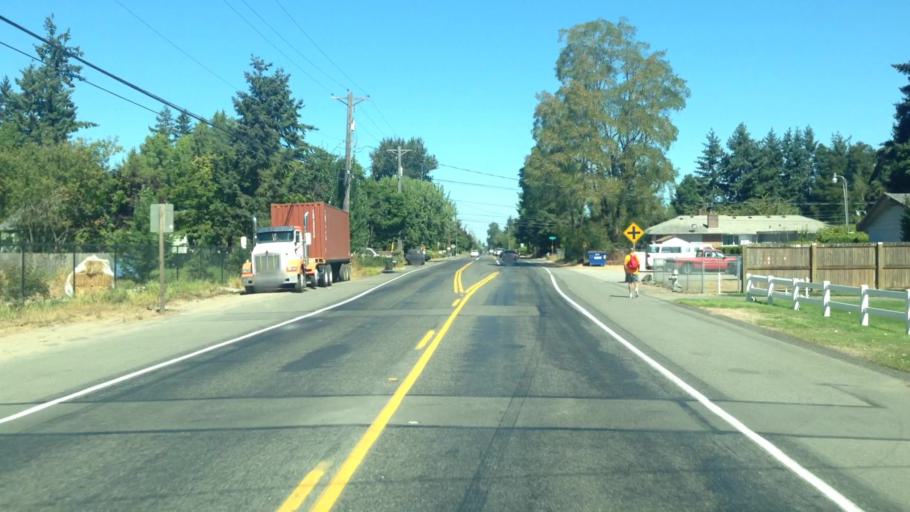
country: US
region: Washington
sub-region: Pierce County
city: Midland
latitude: 47.1612
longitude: -122.4155
